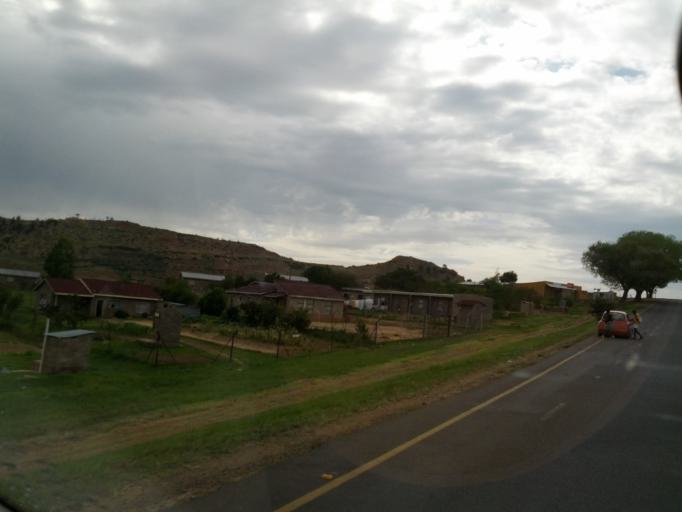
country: LS
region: Maseru
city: Maseru
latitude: -29.4119
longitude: 27.6235
